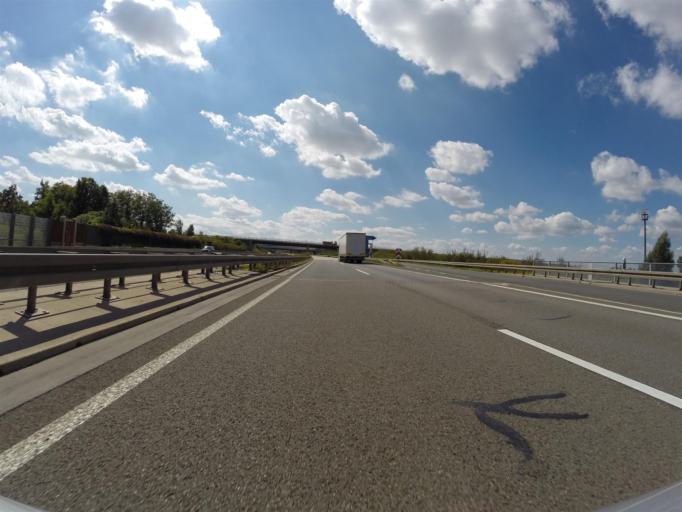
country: DE
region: Thuringia
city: Elxleben
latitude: 51.0276
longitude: 10.9804
